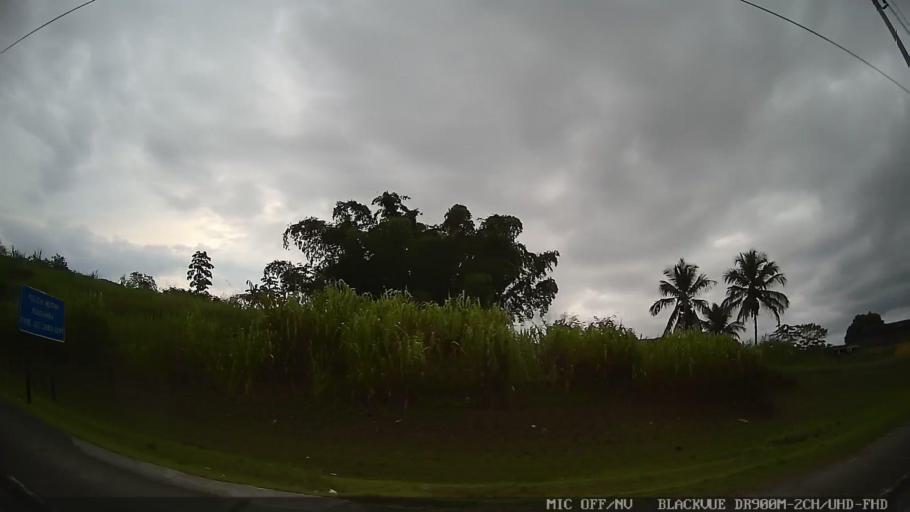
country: BR
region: Sao Paulo
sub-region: Caraguatatuba
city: Caraguatatuba
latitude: -23.6179
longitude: -45.4309
